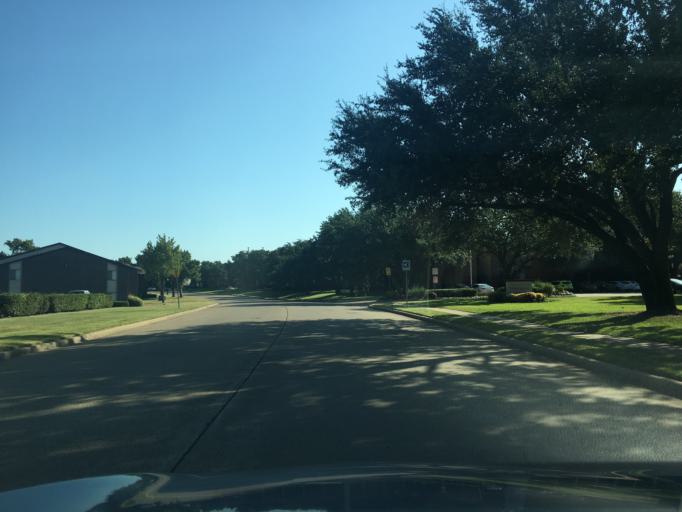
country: US
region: Texas
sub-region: Dallas County
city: Addison
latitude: 32.9616
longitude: -96.8502
